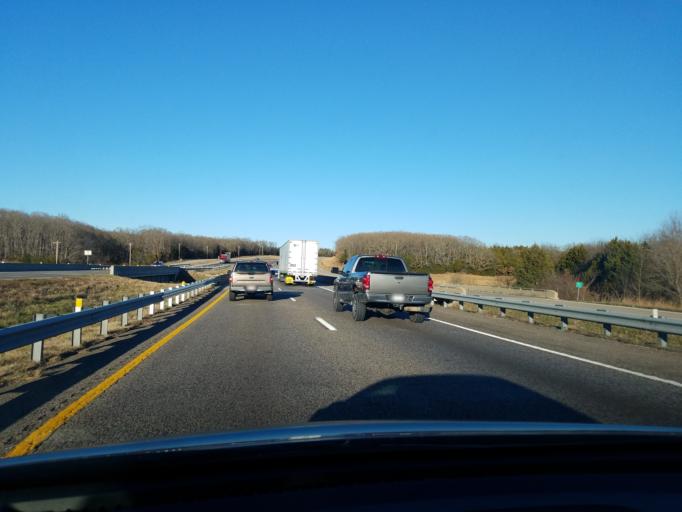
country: US
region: Missouri
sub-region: Franklin County
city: Sullivan
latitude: 38.2487
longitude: -91.1356
